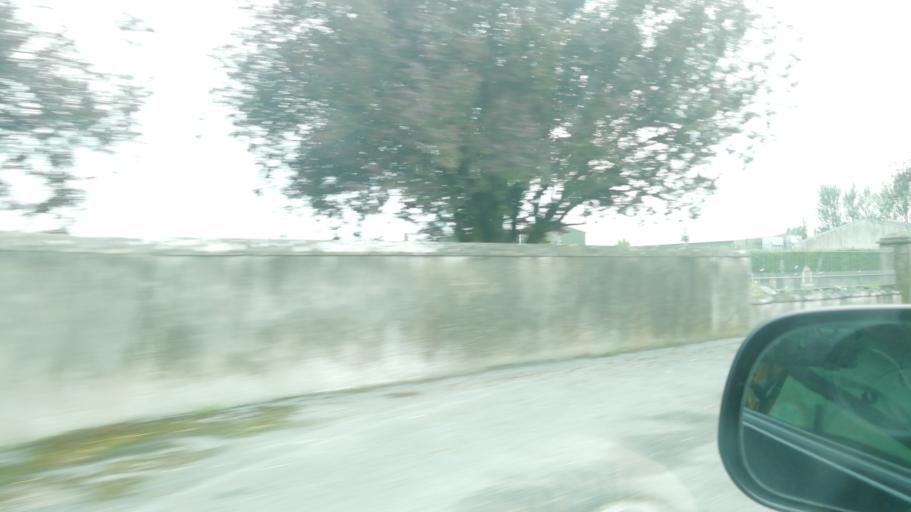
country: IE
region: Munster
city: Fethard
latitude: 52.4748
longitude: -7.6920
